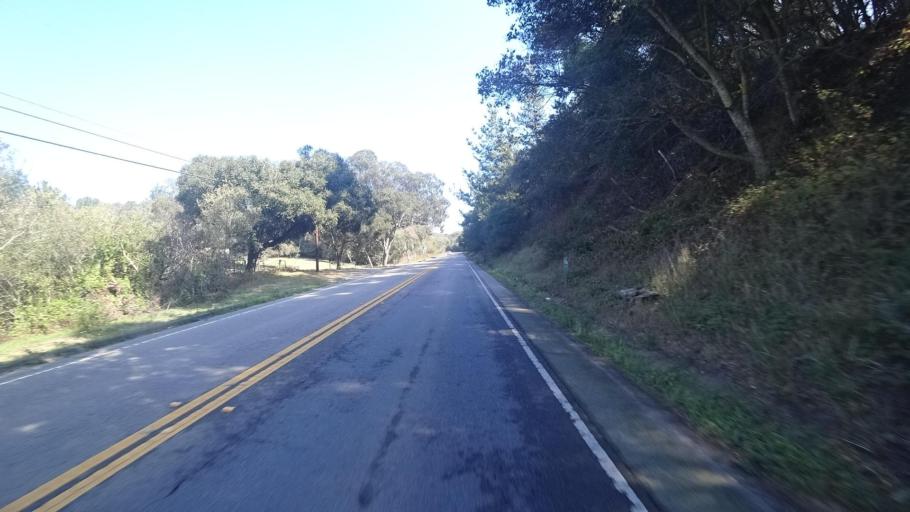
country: US
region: California
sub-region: Monterey County
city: Prunedale
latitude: 36.8003
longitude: -121.6927
